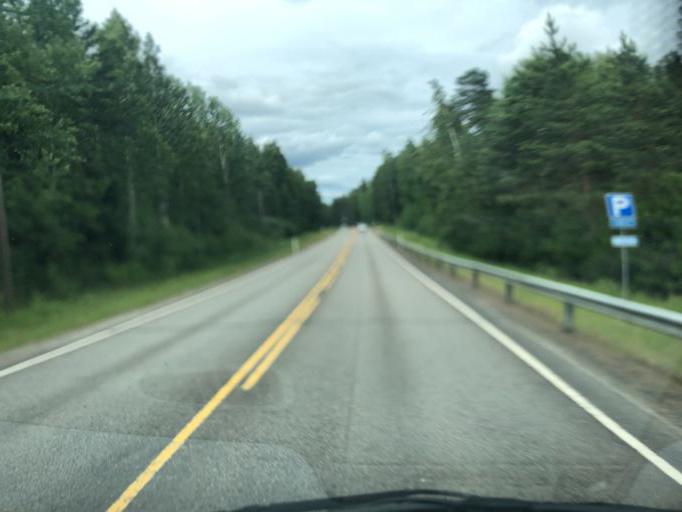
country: FI
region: Kymenlaakso
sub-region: Kouvola
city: Kouvola
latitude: 60.9552
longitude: 26.8582
